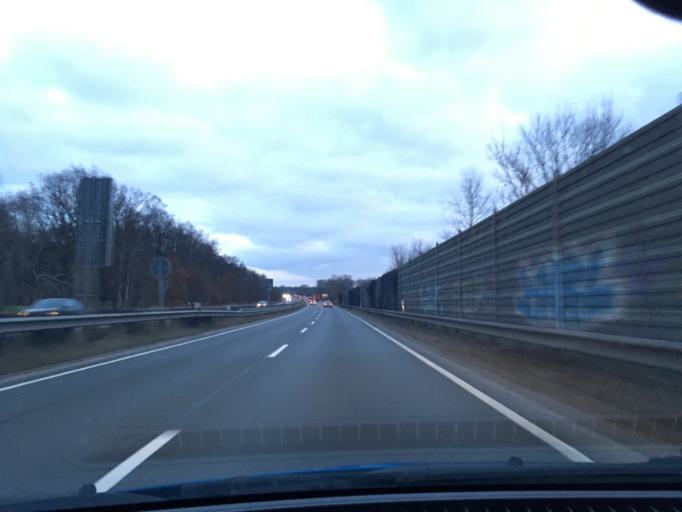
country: DE
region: Lower Saxony
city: Lueneburg
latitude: 53.2754
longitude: 10.4079
